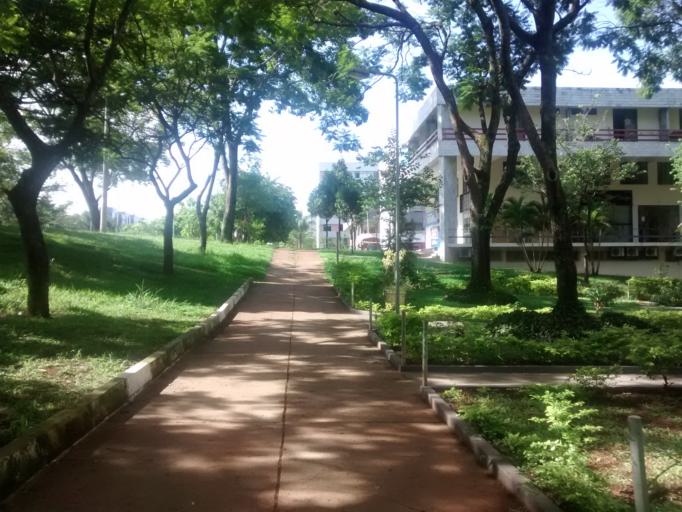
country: BR
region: Federal District
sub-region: Brasilia
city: Brasilia
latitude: -15.7474
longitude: -47.8922
